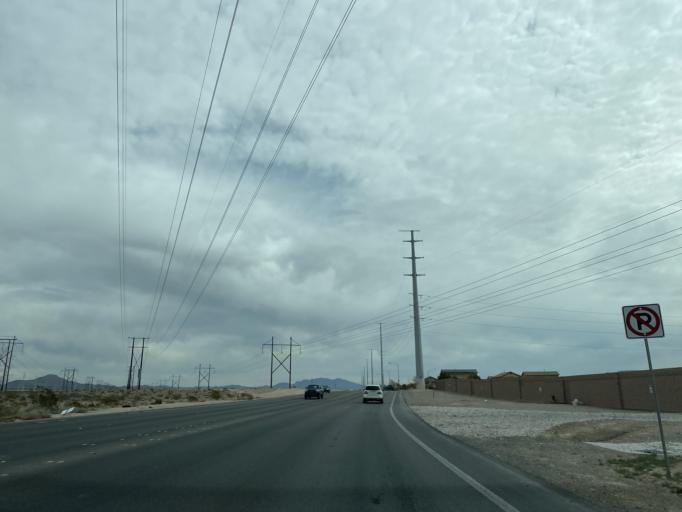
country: US
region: Nevada
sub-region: Clark County
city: Nellis Air Force Base
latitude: 36.2766
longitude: -115.0961
